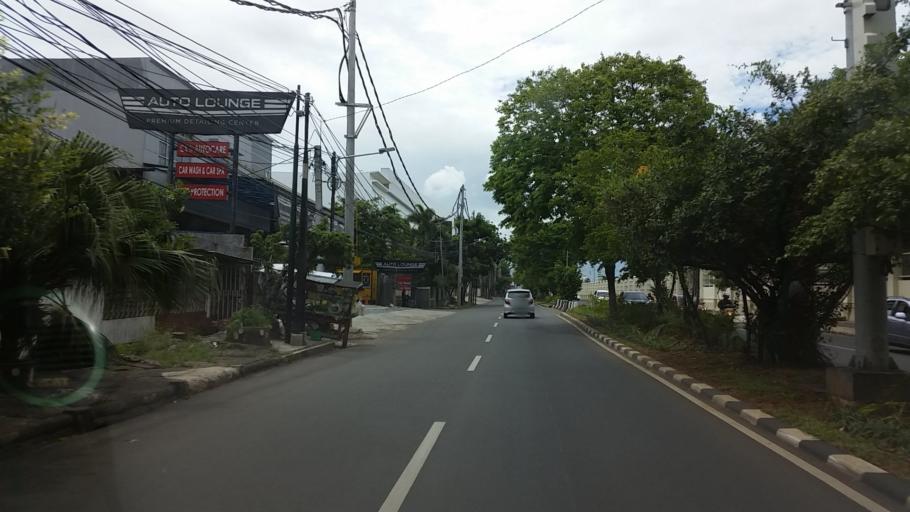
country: ID
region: Jakarta Raya
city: Jakarta
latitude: -6.1123
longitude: 106.7886
